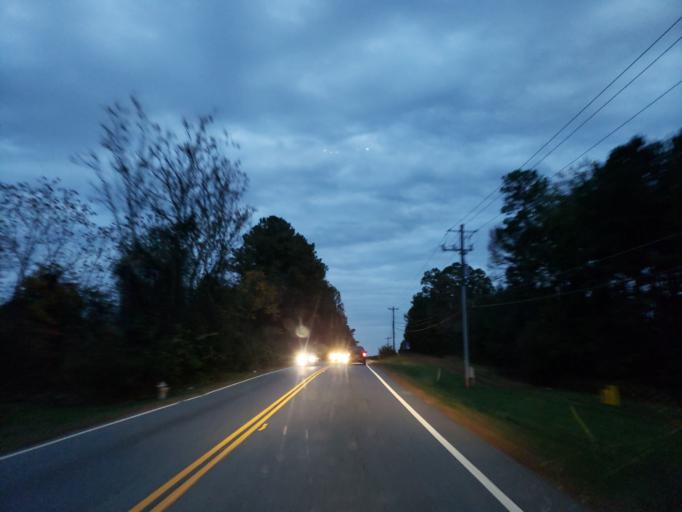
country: US
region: Georgia
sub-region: Cobb County
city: Powder Springs
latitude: 33.9375
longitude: -84.7011
